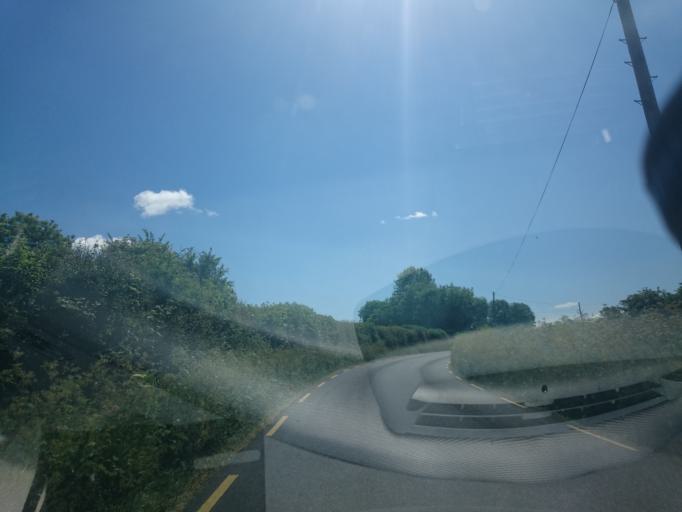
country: IE
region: Leinster
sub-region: Kilkenny
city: Graiguenamanagh
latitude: 52.5977
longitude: -6.9896
